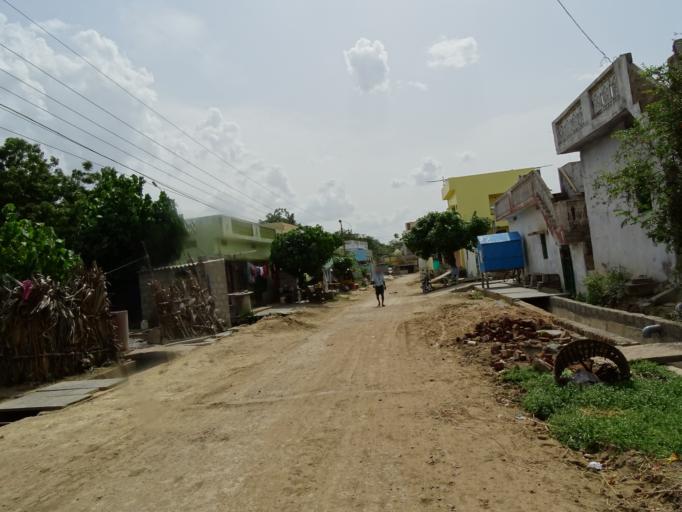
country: IN
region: Andhra Pradesh
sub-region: Krishna
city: Kondapalle
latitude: 16.5313
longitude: 80.4232
